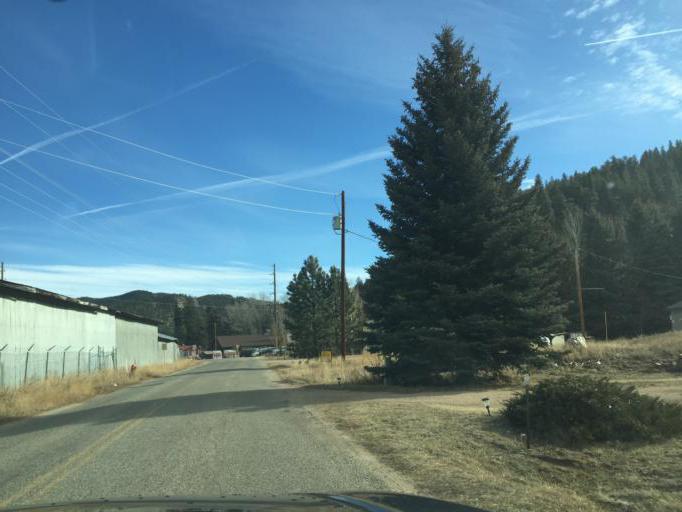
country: US
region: Colorado
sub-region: Jefferson County
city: Evergreen
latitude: 39.4060
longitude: -105.4803
